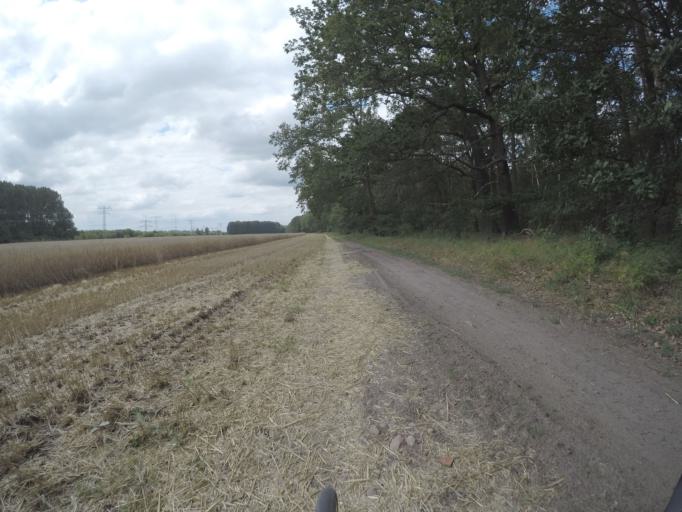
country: DE
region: Brandenburg
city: Brieselang
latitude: 52.6141
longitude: 13.0351
